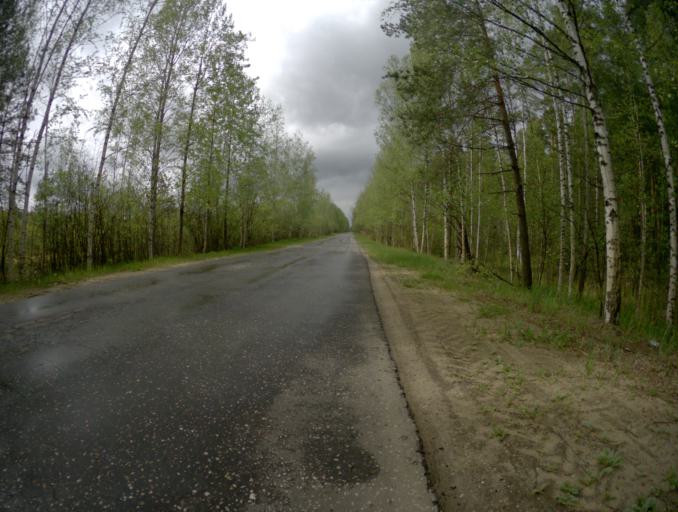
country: RU
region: Vladimir
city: Zolotkovo
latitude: 55.3523
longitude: 40.9204
